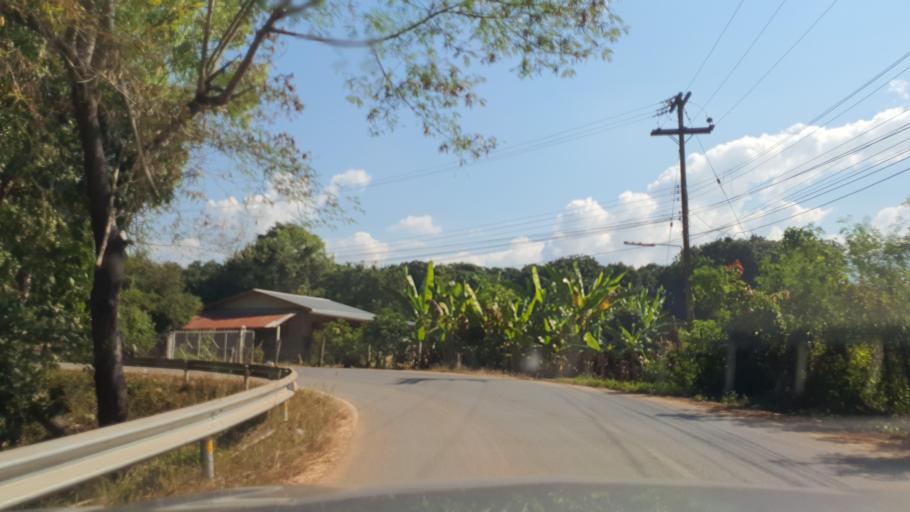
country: TH
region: Nan
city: Pua
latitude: 19.1407
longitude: 100.9259
